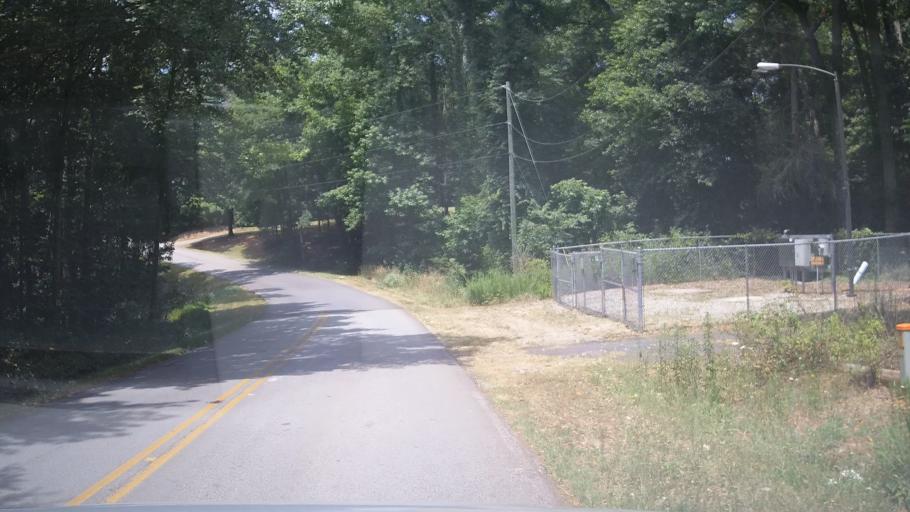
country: US
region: Georgia
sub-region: Hart County
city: Hartwell
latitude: 34.3476
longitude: -82.9071
